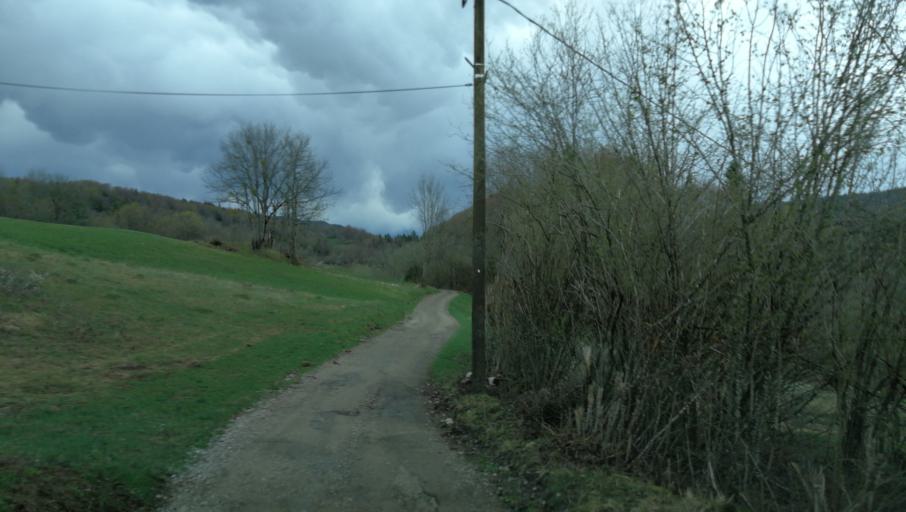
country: FR
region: Franche-Comte
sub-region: Departement du Jura
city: Lavans-les-Saint-Claude
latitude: 46.3147
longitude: 5.8060
